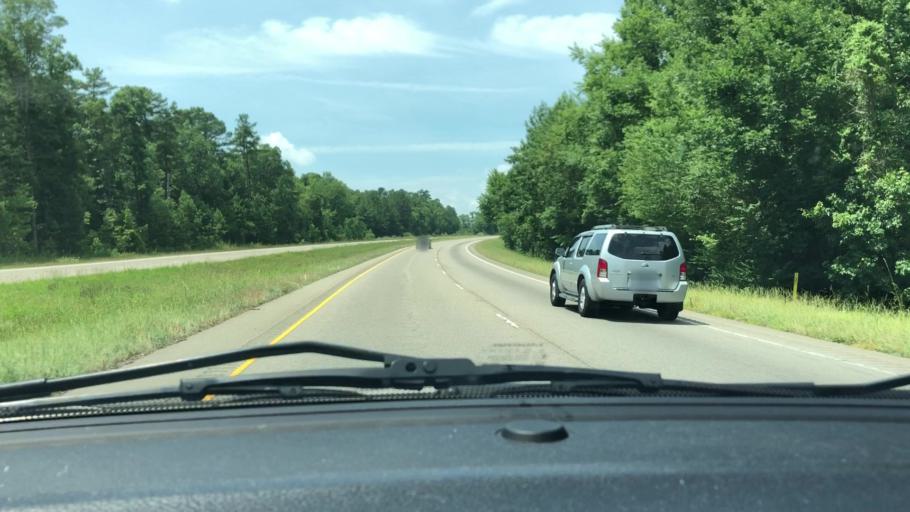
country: US
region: North Carolina
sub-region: Chatham County
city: Farmville
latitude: 35.5728
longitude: -79.3074
